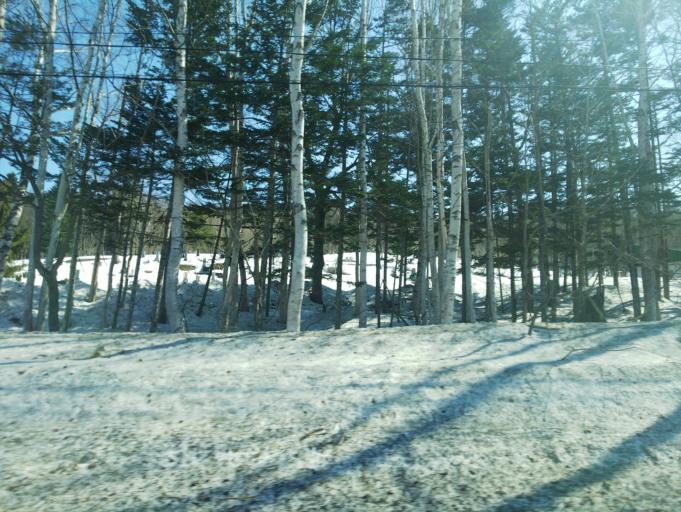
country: JP
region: Hokkaido
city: Nayoro
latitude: 44.7180
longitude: 142.2715
